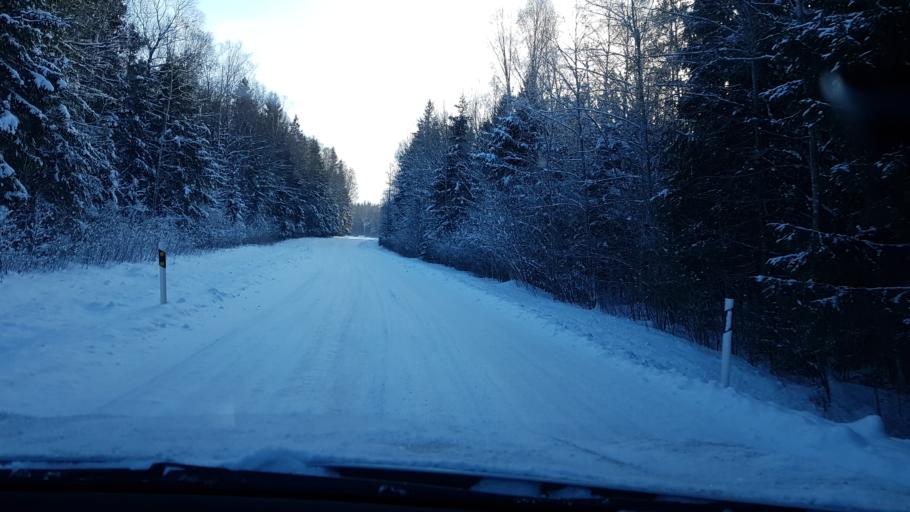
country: EE
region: Harju
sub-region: Nissi vald
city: Turba
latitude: 59.1316
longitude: 24.1958
